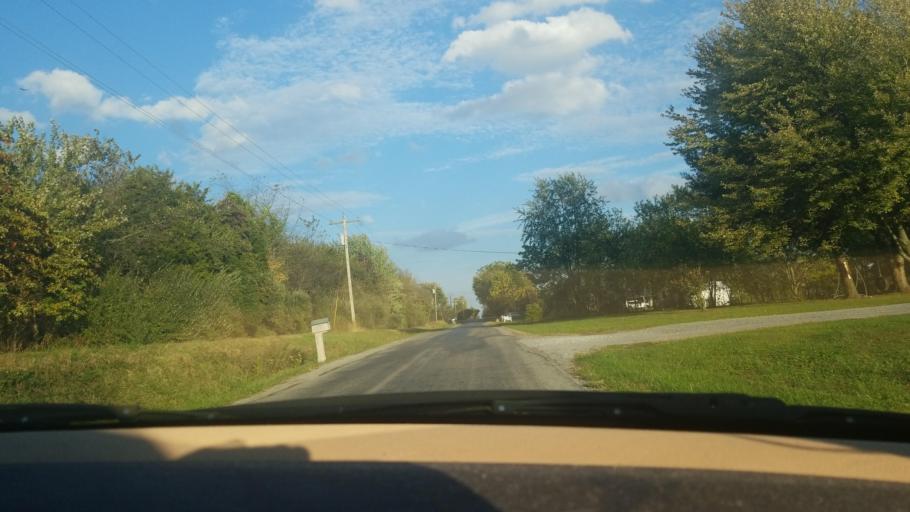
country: US
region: Illinois
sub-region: Saline County
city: Carrier Mills
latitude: 37.7719
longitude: -88.7329
